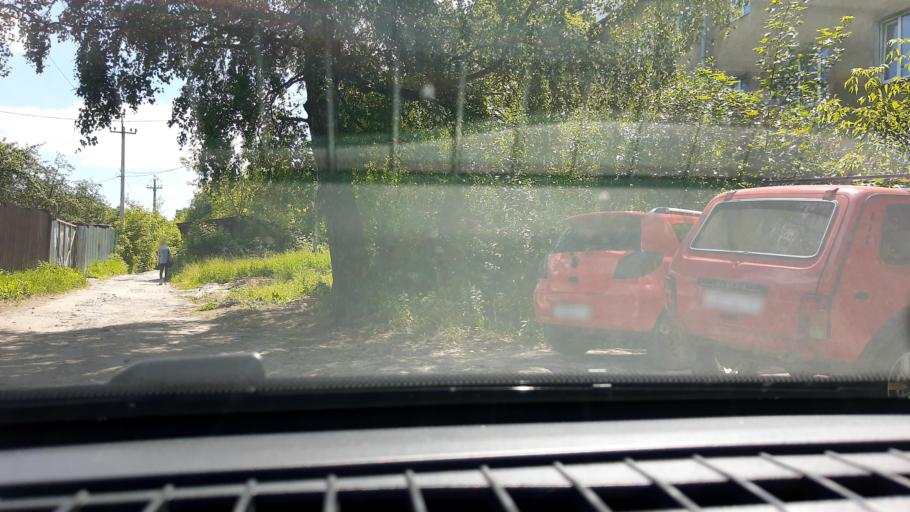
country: RU
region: Nizjnij Novgorod
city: Nizhniy Novgorod
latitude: 56.2627
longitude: 43.9894
